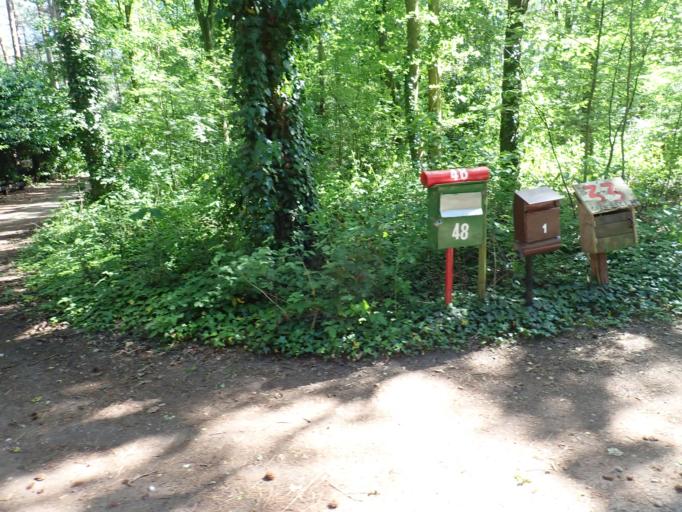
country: BE
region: Flanders
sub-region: Provincie Antwerpen
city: Kasterlee
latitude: 51.2206
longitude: 4.9261
